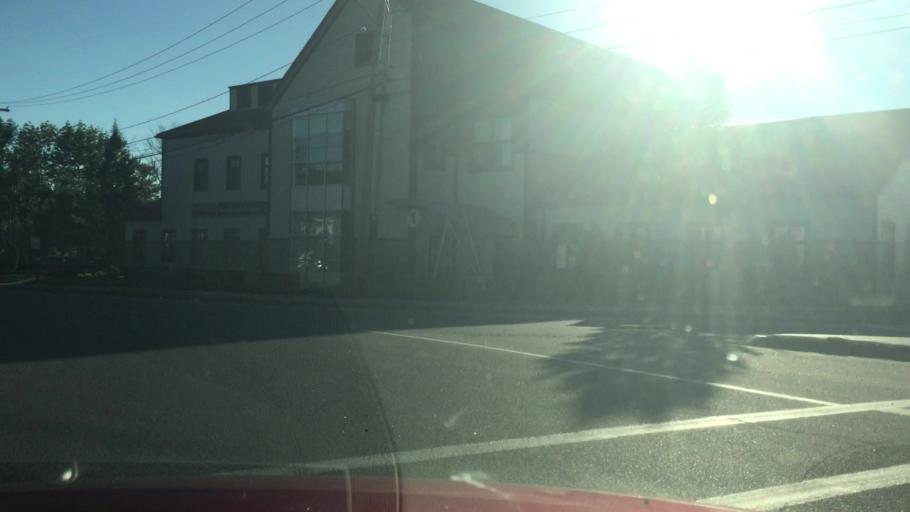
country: US
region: Maine
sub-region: Cumberland County
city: Westbrook
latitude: 43.6823
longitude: -70.3497
